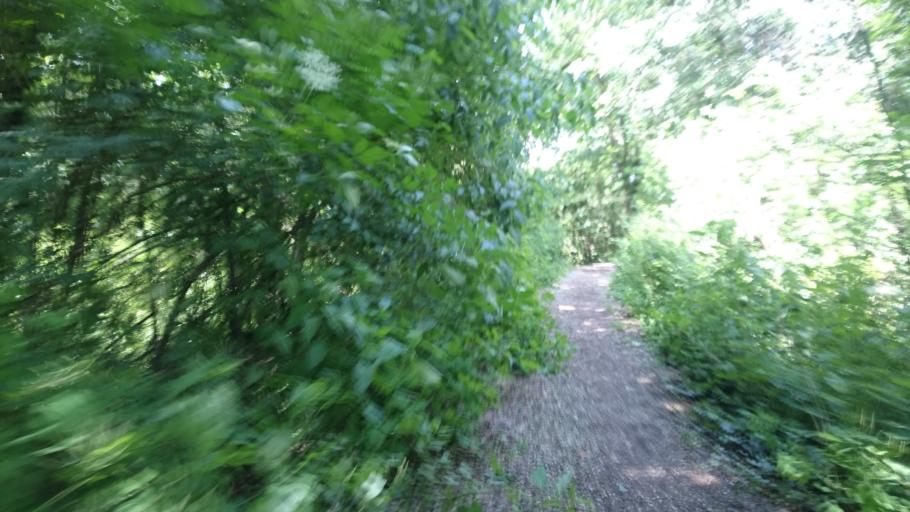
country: IT
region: Lombardy
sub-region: Provincia di Mantova
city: Mantova
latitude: 45.1398
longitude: 10.8051
